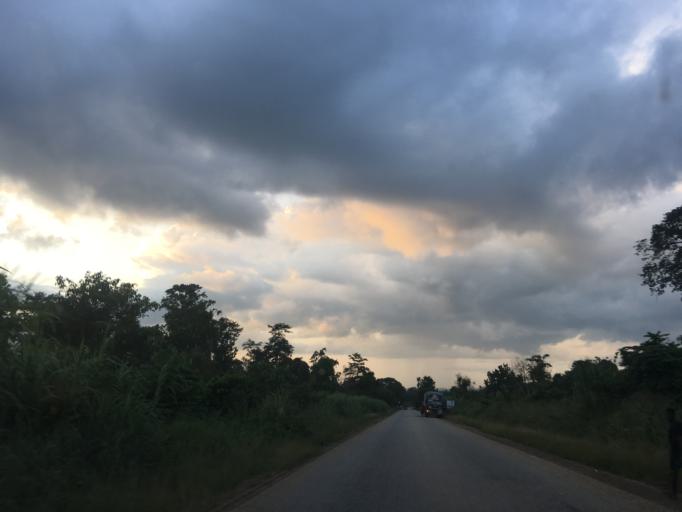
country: GH
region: Western
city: Bibiani
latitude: 6.7445
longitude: -2.5039
